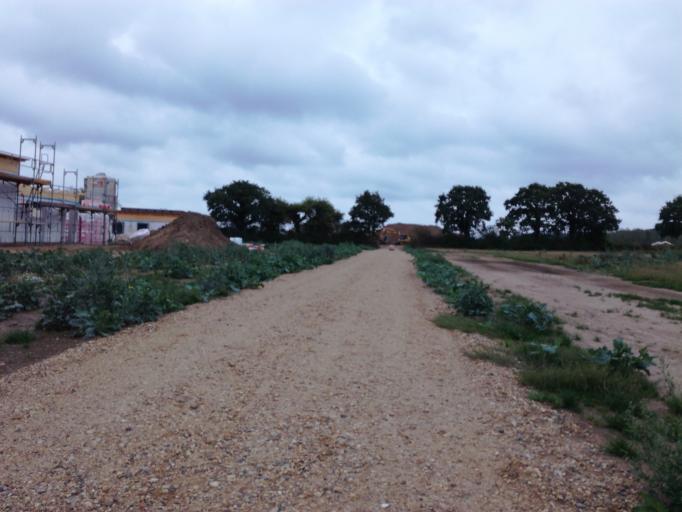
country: DK
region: South Denmark
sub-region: Vejle Kommune
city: Borkop
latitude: 55.6344
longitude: 9.6402
